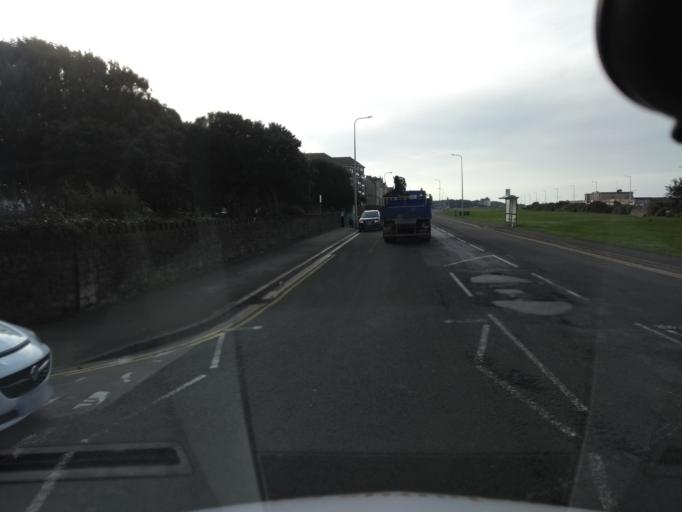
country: GB
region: England
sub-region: North Somerset
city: Weston-super-Mare
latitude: 51.3429
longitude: -2.9806
